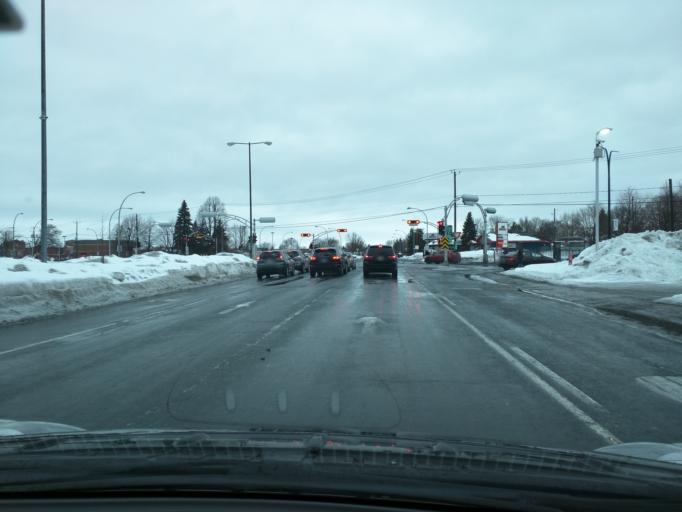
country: CA
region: Quebec
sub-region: Monteregie
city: Longueuil
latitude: 45.5215
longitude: -73.4641
